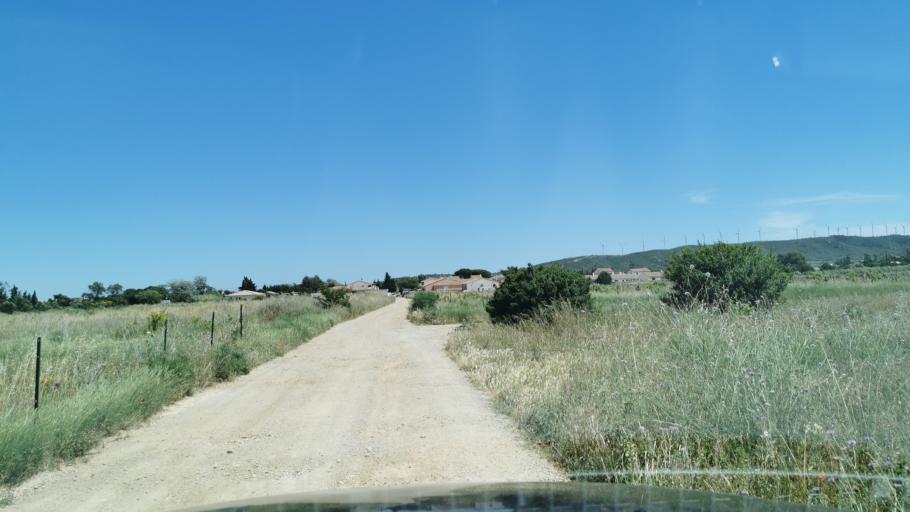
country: FR
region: Languedoc-Roussillon
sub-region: Departement de l'Aude
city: Canet
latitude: 43.2176
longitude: 2.8499
